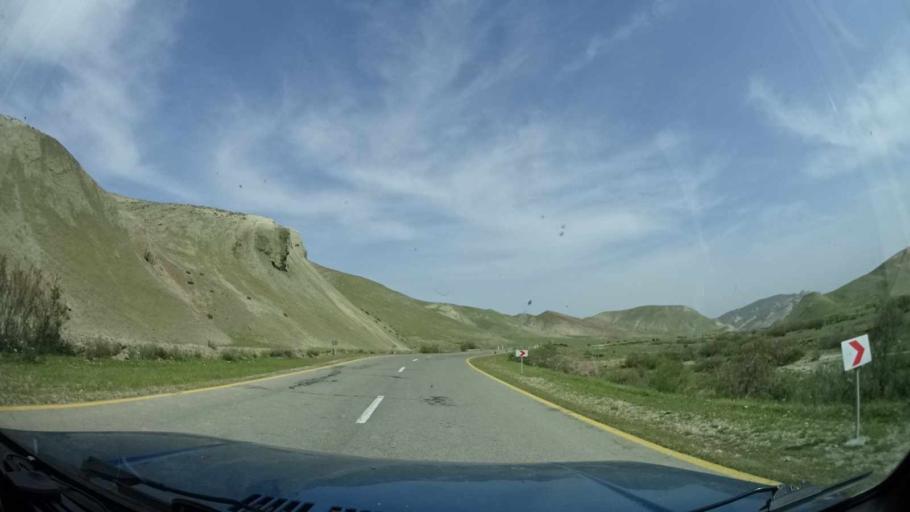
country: AZ
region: Xizi
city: Kilyazi
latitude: 40.8667
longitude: 49.2164
